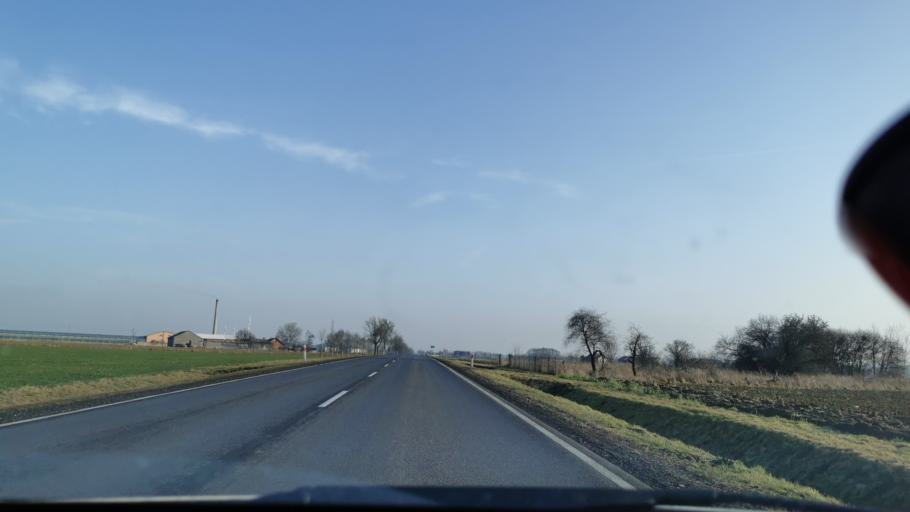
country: PL
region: Lodz Voivodeship
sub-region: Powiat sieradzki
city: Blaszki
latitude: 51.6814
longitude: 18.3405
